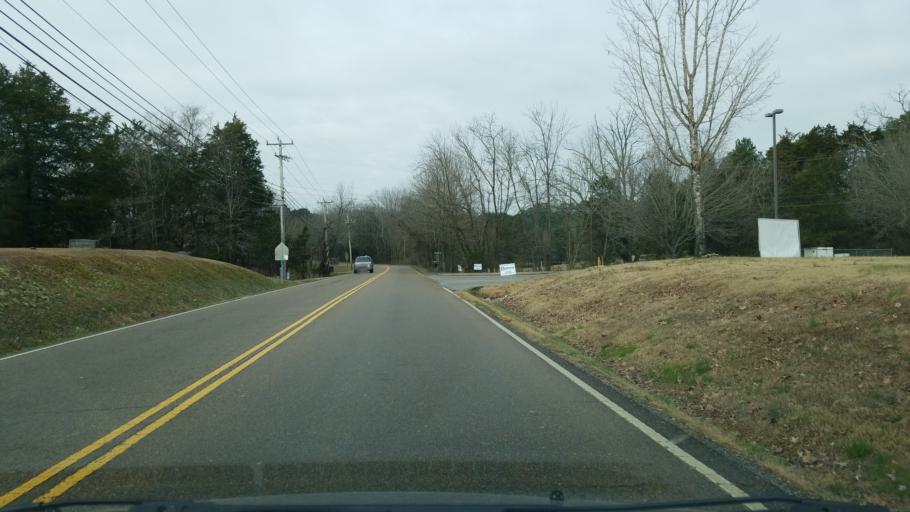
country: US
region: Tennessee
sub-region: Hamilton County
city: East Brainerd
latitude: 35.0009
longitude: -85.0987
